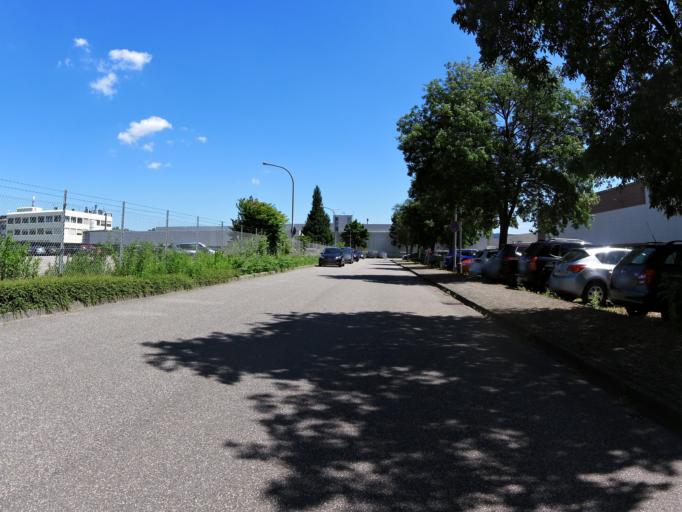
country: DE
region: Baden-Wuerttemberg
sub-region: Freiburg Region
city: Lahr
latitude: 48.3445
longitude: 7.8264
